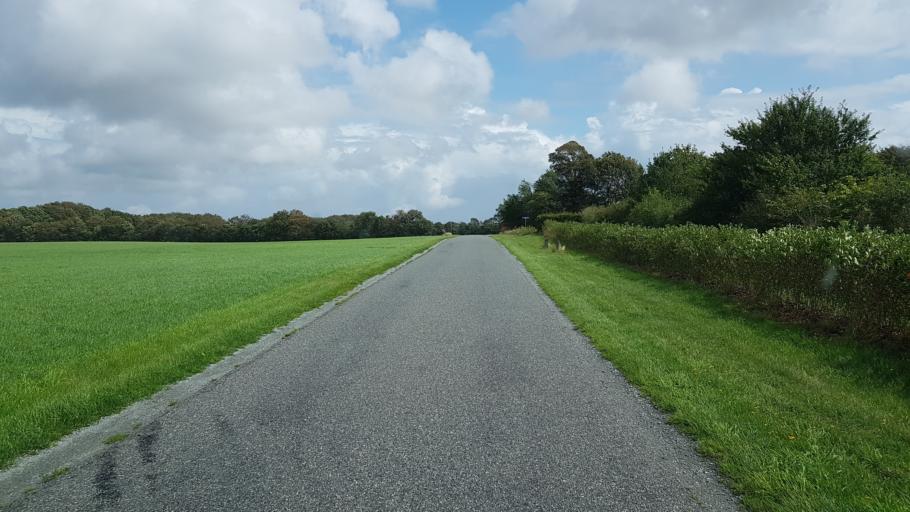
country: DK
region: South Denmark
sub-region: Vejen Kommune
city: Holsted
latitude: 55.4948
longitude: 8.9485
